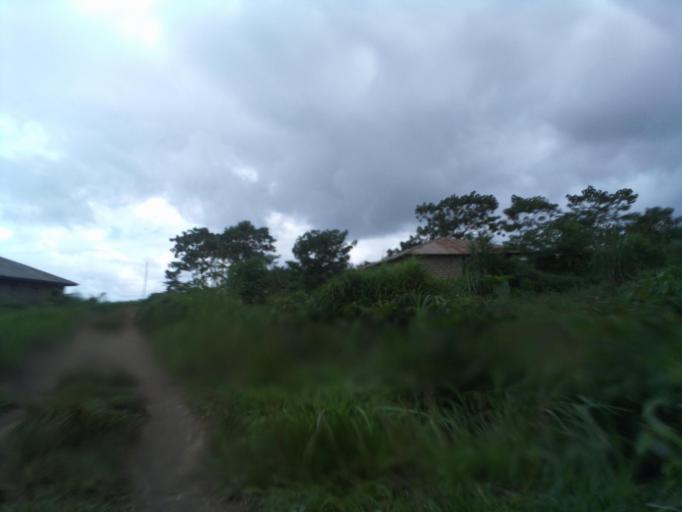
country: SL
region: Eastern Province
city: Kenema
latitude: 7.8362
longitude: -11.1808
